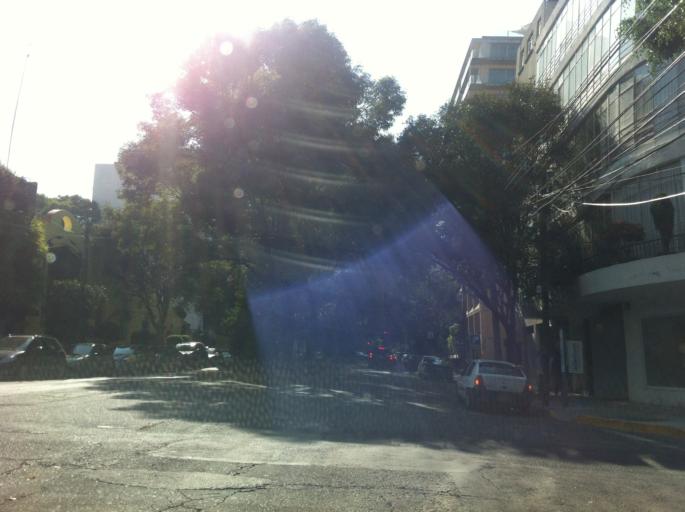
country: MX
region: Mexico City
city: Miguel Hidalgo
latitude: 19.4291
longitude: -99.1904
